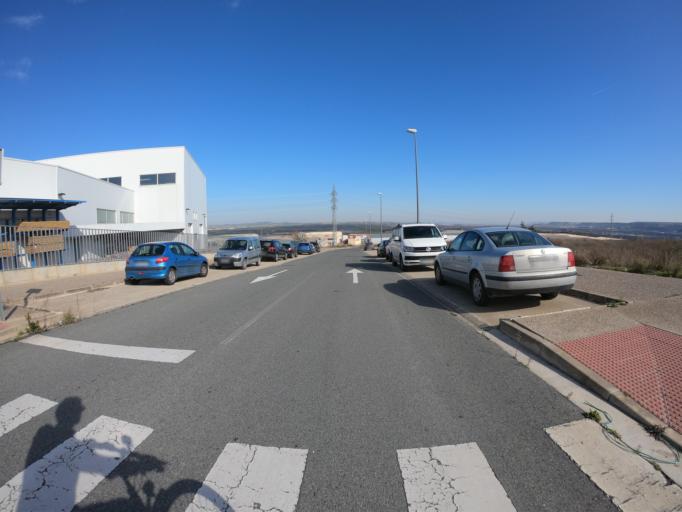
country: ES
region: Basque Country
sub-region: Provincia de Alava
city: Oyon
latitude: 42.4781
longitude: -2.4192
